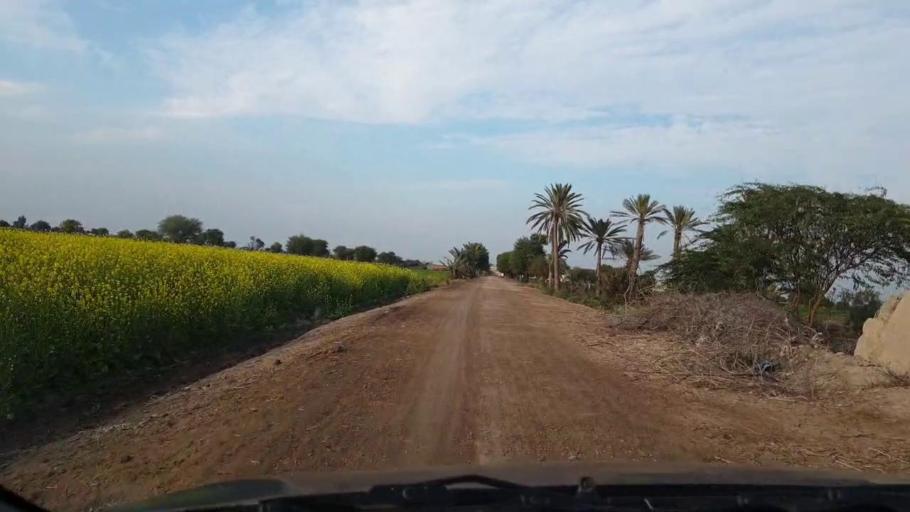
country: PK
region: Sindh
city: Jhol
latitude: 25.9767
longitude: 68.8736
